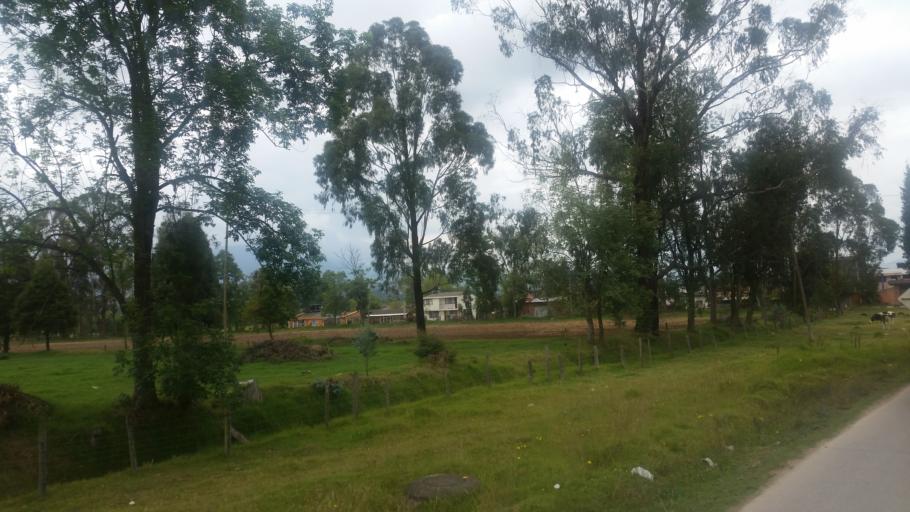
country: CO
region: Cundinamarca
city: Cogua
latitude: 5.0410
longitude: -73.9553
